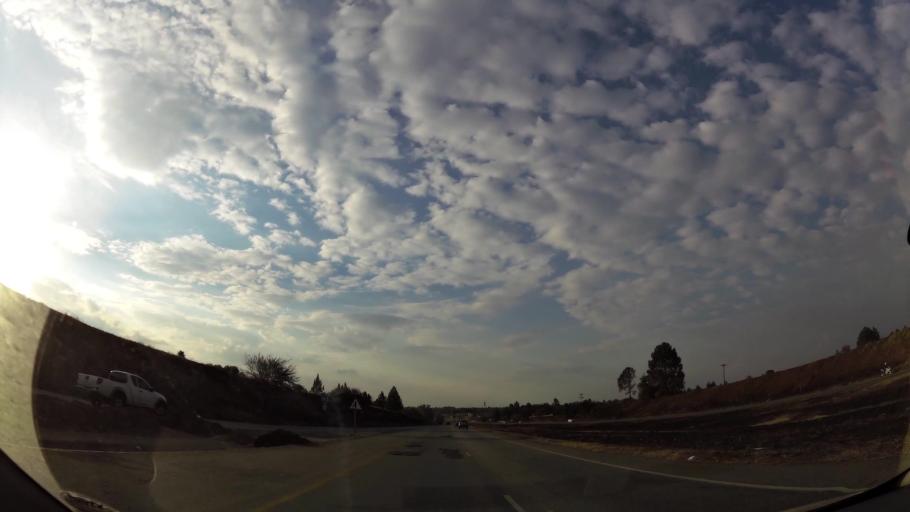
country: ZA
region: Gauteng
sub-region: Sedibeng District Municipality
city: Vanderbijlpark
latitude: -26.7543
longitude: 27.8255
